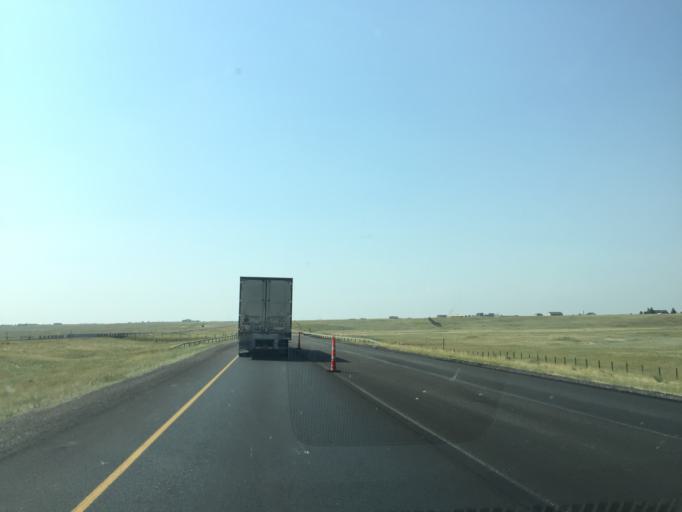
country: US
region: Wyoming
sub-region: Laramie County
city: Ranchettes
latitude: 41.3123
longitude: -104.8582
